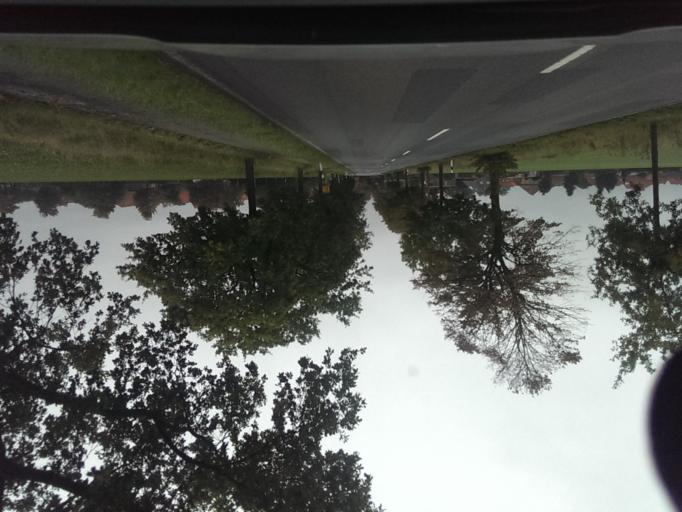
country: DE
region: Lower Saxony
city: Gross Munzel
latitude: 52.3671
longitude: 9.4954
